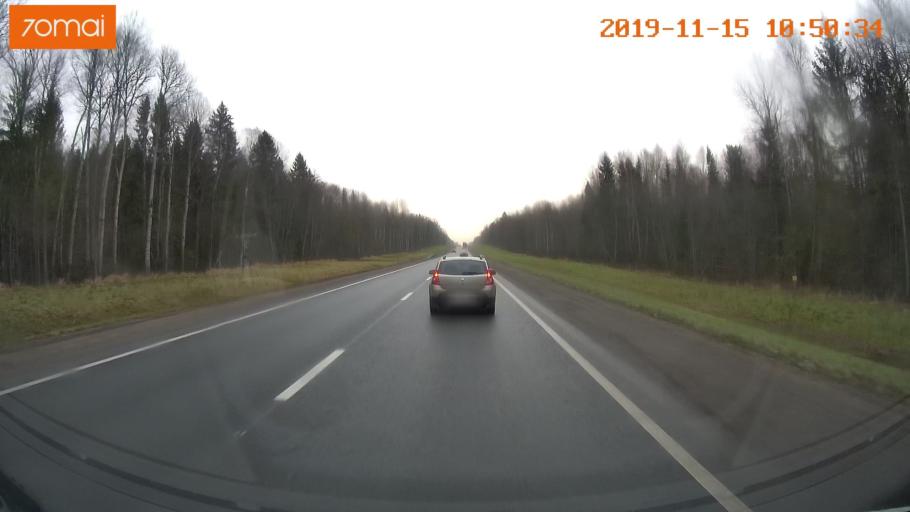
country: RU
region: Vologda
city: Chebsara
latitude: 59.1846
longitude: 38.6846
